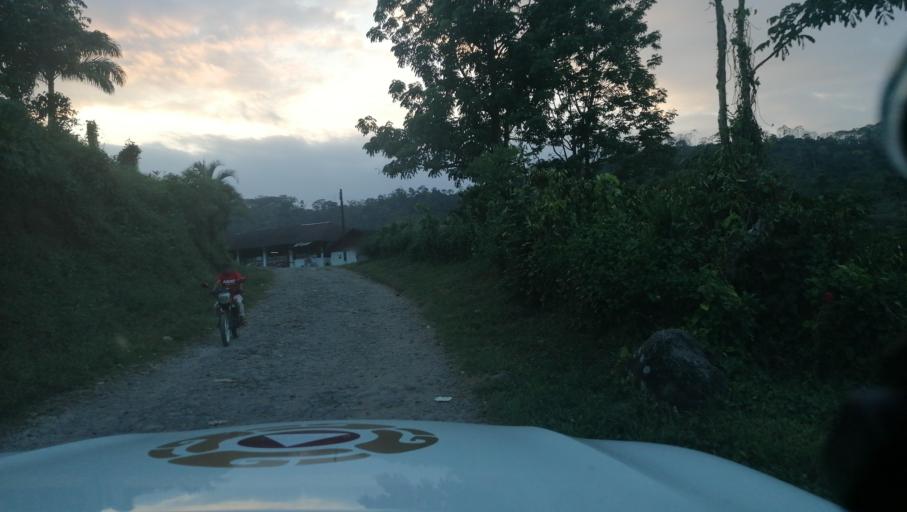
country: MX
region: Chiapas
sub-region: Cacahoatan
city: Benito Juarez
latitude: 15.0649
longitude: -92.2362
